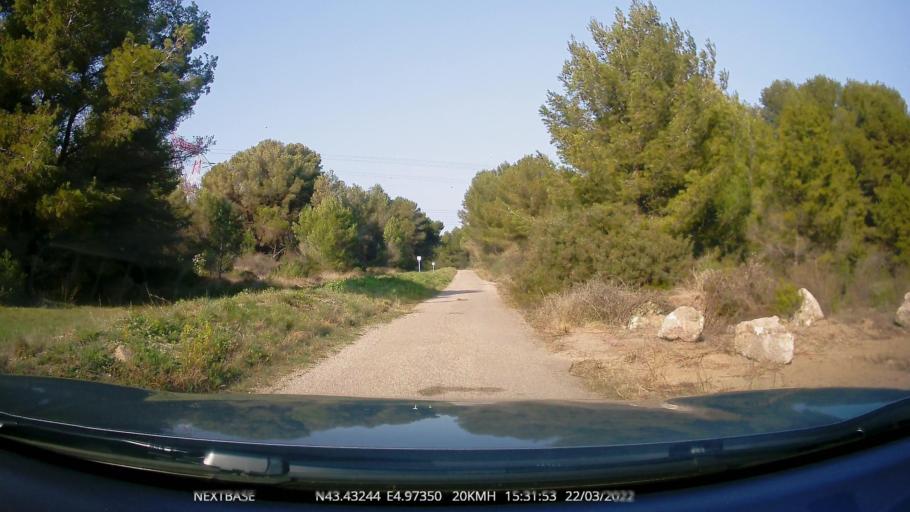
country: FR
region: Provence-Alpes-Cote d'Azur
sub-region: Departement des Bouches-du-Rhone
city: Port-de-Bouc
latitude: 43.4322
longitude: 4.9733
